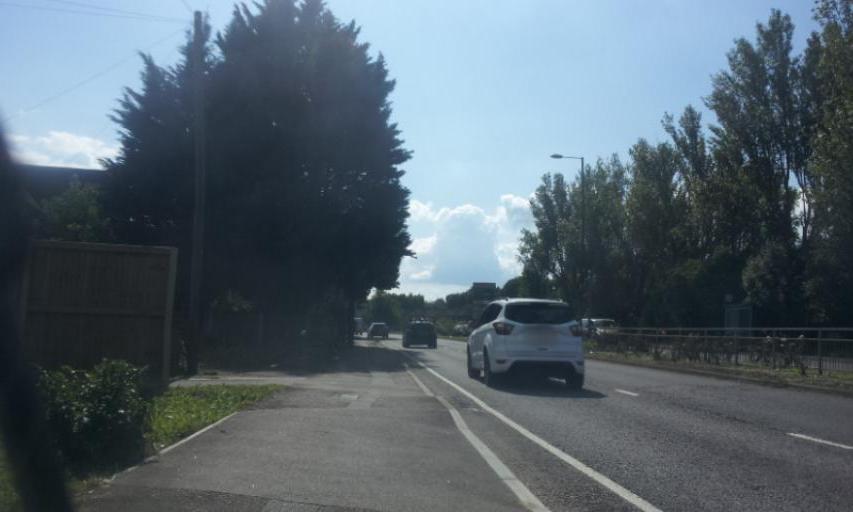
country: GB
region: England
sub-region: Kent
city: Chatham
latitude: 51.3467
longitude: 0.5079
